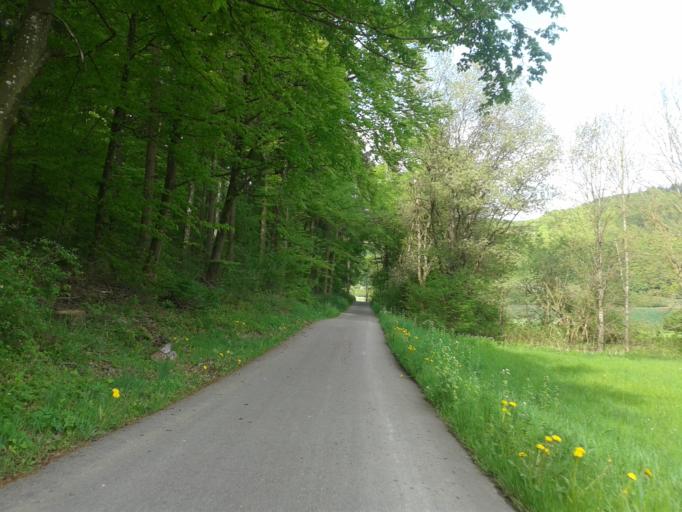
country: DE
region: Baden-Wuerttemberg
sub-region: Tuebingen Region
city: Blaubeuren
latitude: 48.4083
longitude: 9.8421
